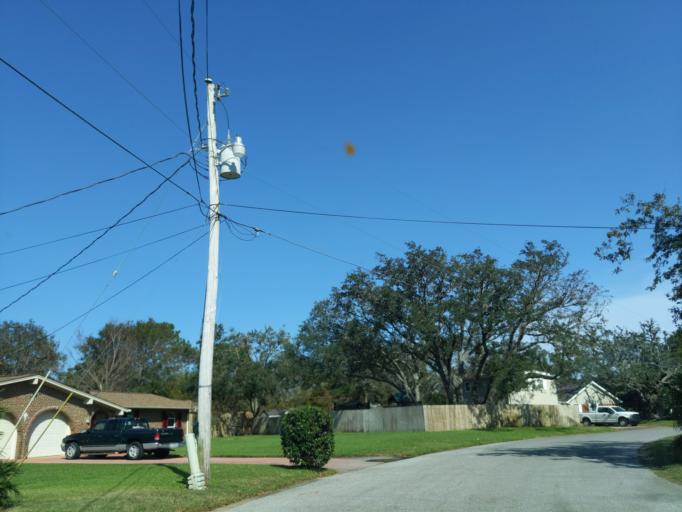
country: US
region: Florida
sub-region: Santa Rosa County
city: Gulf Breeze
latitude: 30.3597
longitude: -87.1813
